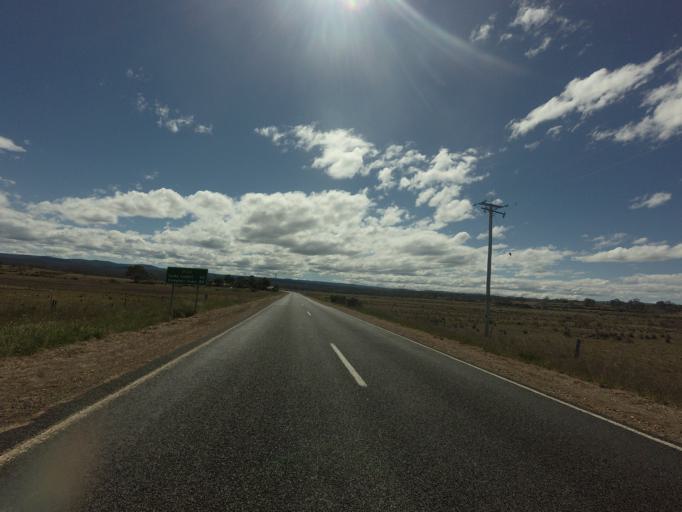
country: AU
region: Tasmania
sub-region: Break O'Day
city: St Helens
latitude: -42.0488
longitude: 148.0484
